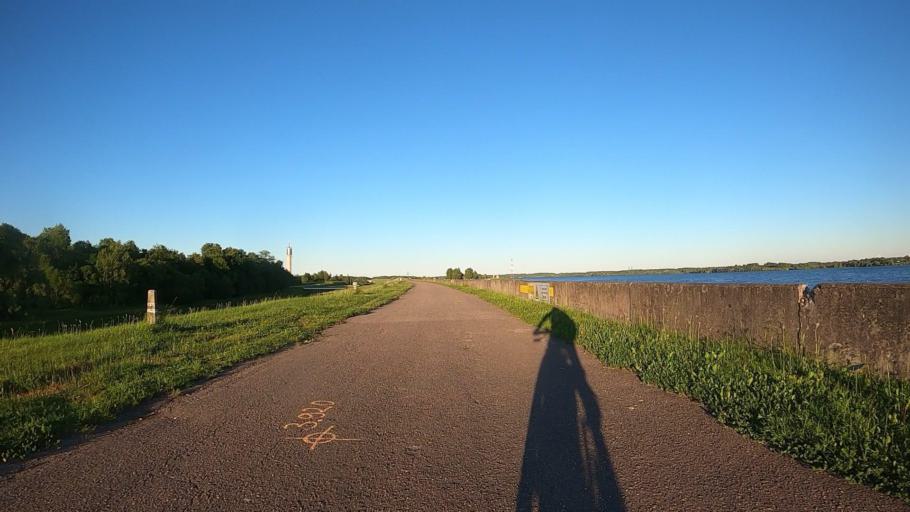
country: LV
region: Salaspils
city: Salaspils
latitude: 56.8489
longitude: 24.3295
